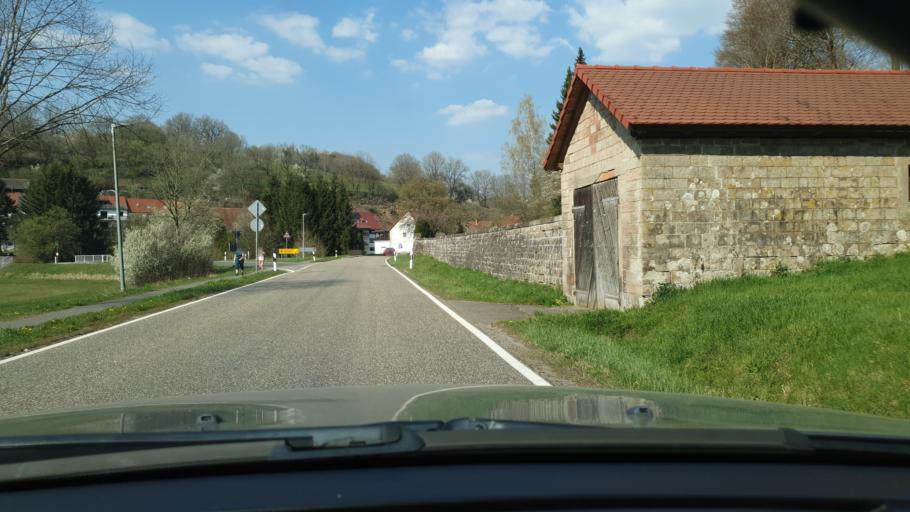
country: DE
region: Rheinland-Pfalz
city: Battweiler
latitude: 49.3002
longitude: 7.4685
